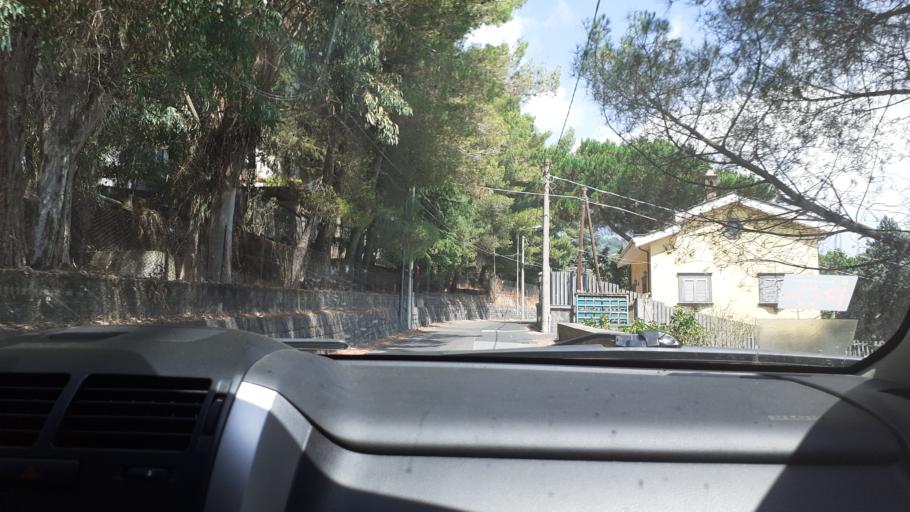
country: IT
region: Sicily
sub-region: Catania
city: Nicolosi
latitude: 37.6250
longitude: 15.0248
